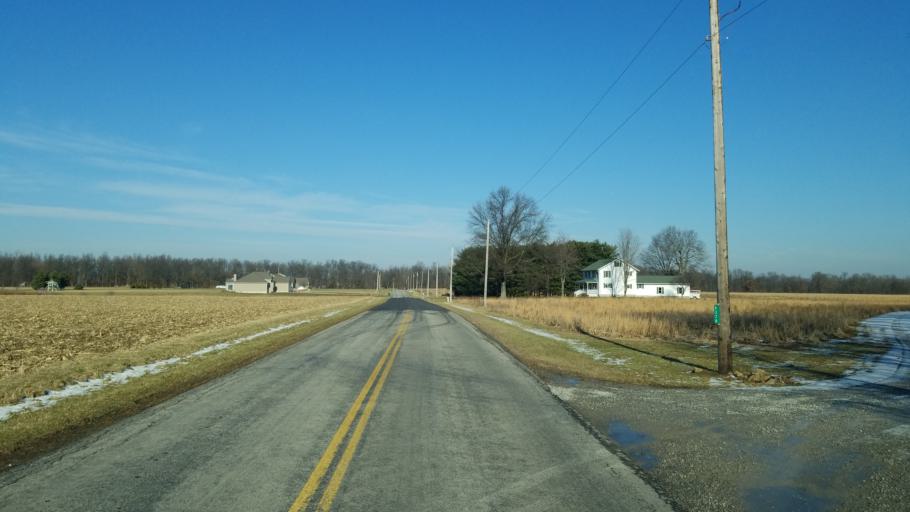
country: US
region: Ohio
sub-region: Huron County
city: Monroeville
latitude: 41.2592
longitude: -82.6896
